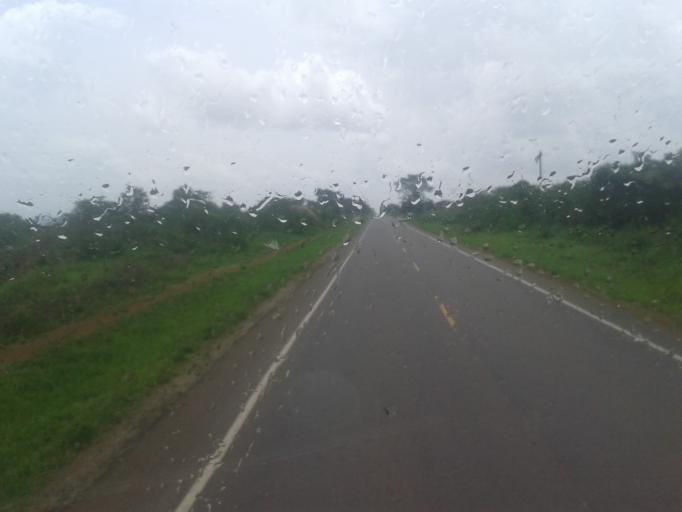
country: UG
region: Western Region
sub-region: Kiryandongo District
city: Masindi Port
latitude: 1.7106
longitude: 32.0284
